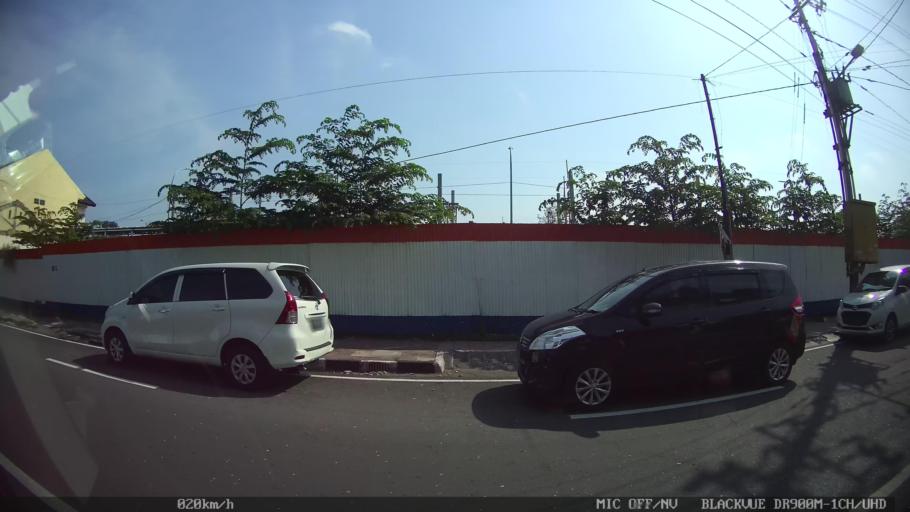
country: ID
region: Daerah Istimewa Yogyakarta
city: Yogyakarta
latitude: -7.7894
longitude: 110.3613
